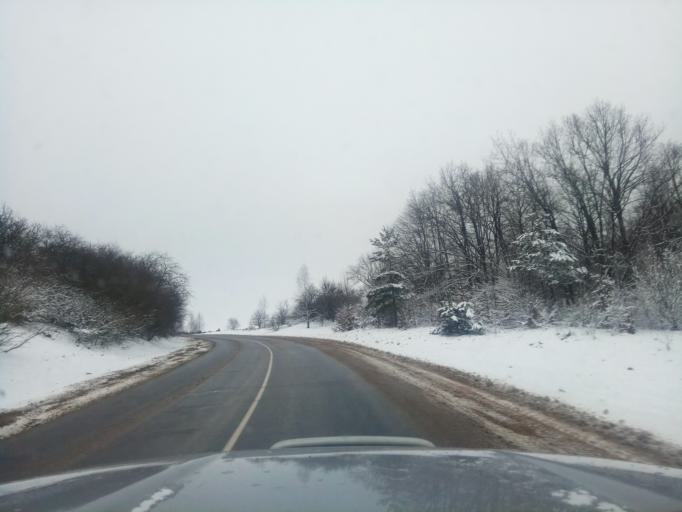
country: BY
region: Minsk
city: Kapyl'
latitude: 53.1549
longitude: 27.1182
